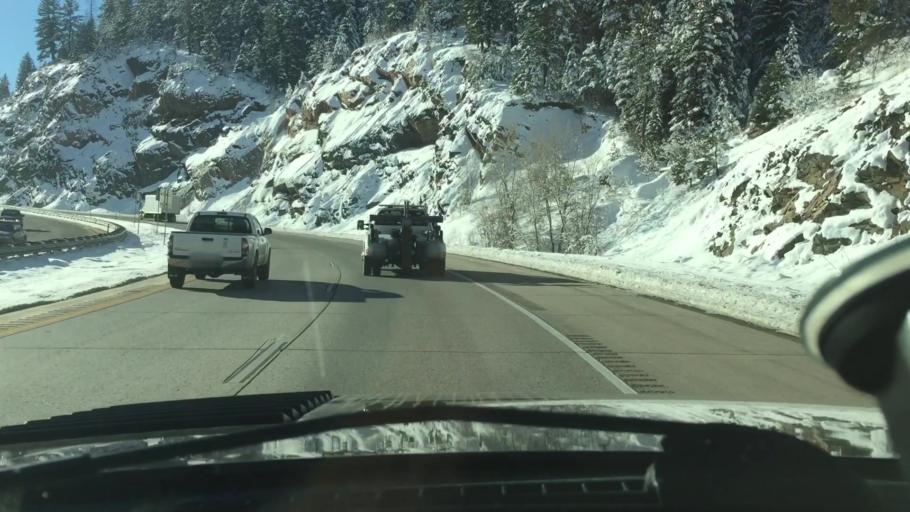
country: US
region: Colorado
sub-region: Jefferson County
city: Indian Hills
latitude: 39.6098
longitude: -105.2319
